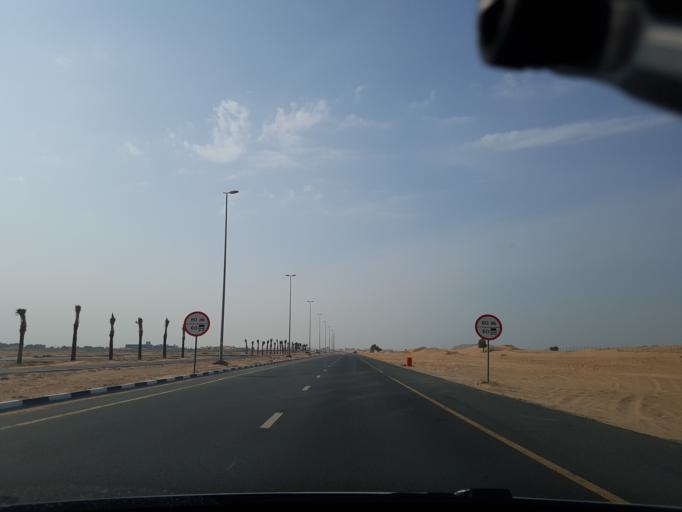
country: AE
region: Ajman
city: Ajman
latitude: 25.4061
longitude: 55.5762
